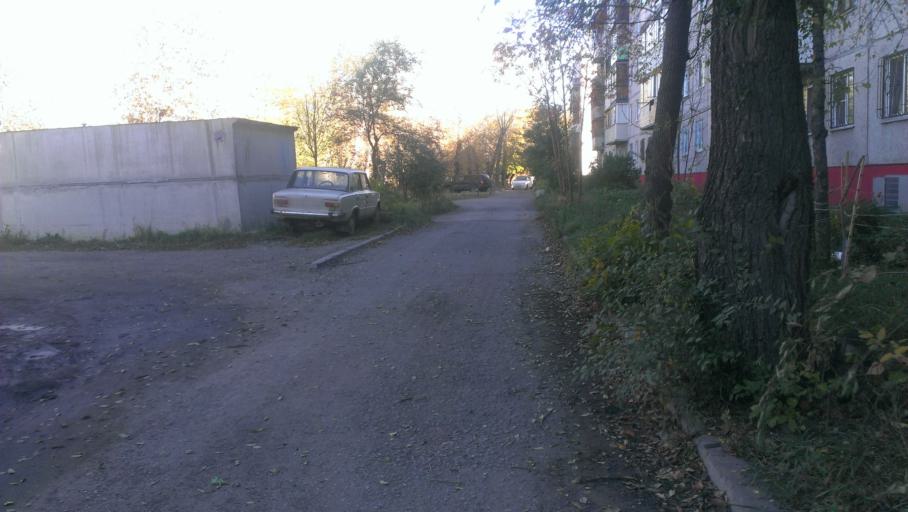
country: RU
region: Altai Krai
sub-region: Gorod Barnaulskiy
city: Barnaul
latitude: 53.3646
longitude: 83.6844
